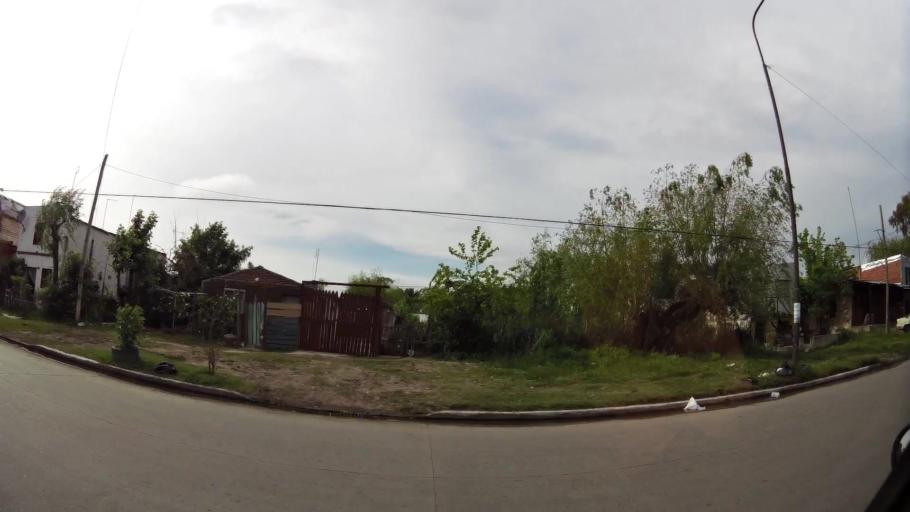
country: AR
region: Buenos Aires
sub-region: Partido de Quilmes
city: Quilmes
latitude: -34.7132
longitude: -58.2281
